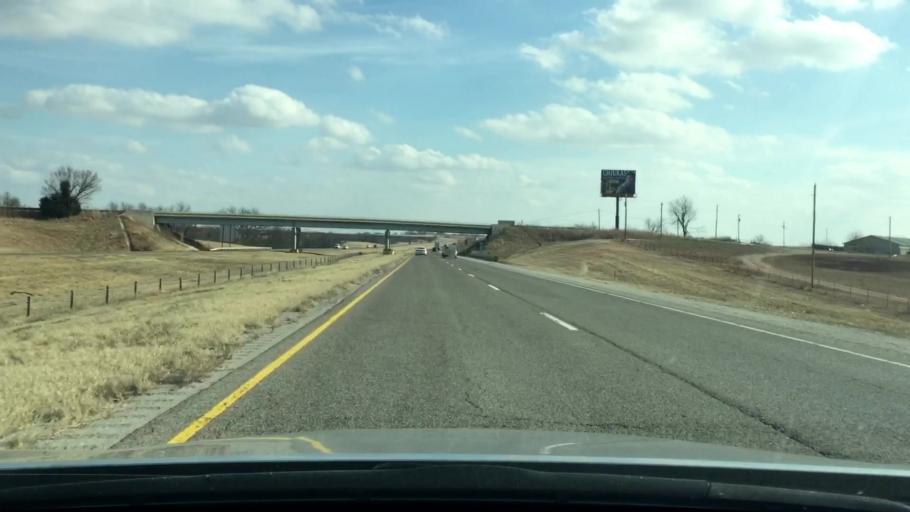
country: US
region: Oklahoma
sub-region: Garvin County
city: Maysville
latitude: 34.8976
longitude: -97.3459
